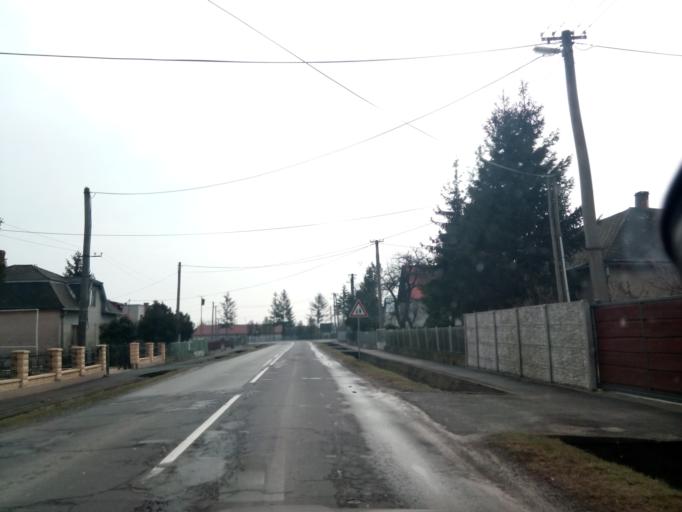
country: SK
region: Kosicky
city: Secovce
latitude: 48.6154
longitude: 21.6017
